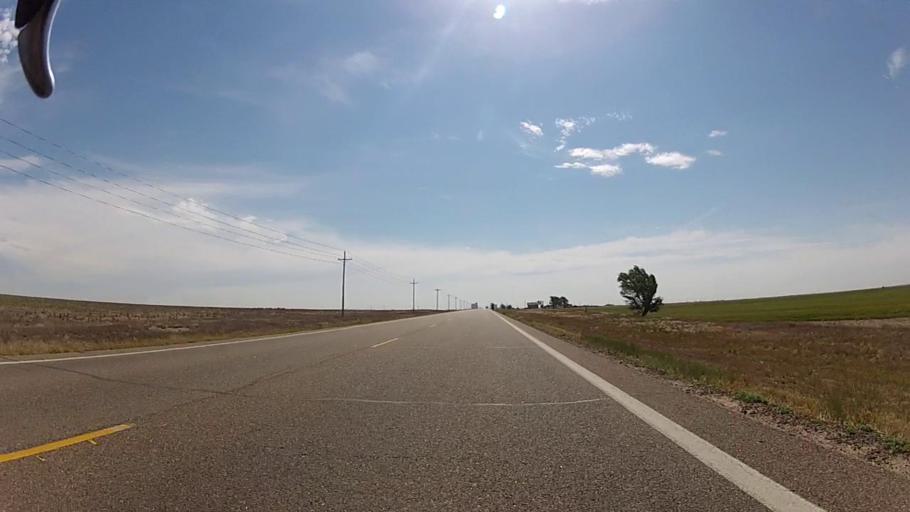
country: US
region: Kansas
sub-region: Grant County
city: Ulysses
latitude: 37.5618
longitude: -101.2681
